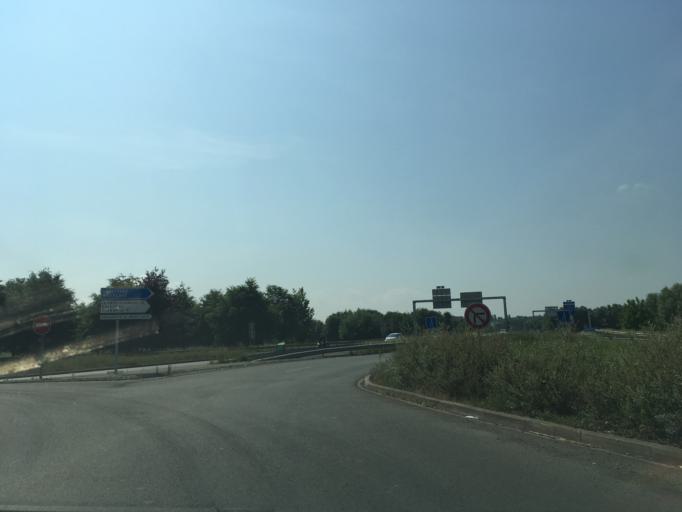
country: FR
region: Nord-Pas-de-Calais
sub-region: Departement du Nord
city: Aulnoy-lez-Valenciennes
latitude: 50.3387
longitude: 3.5130
